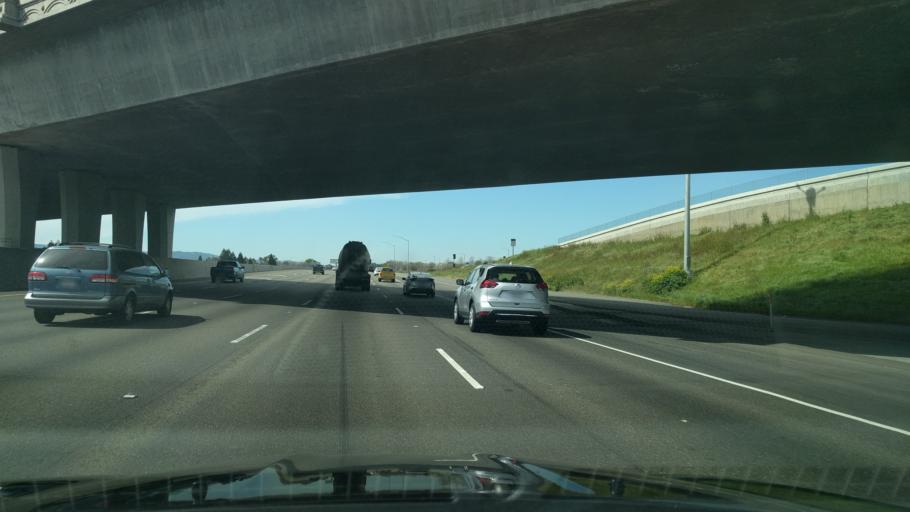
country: US
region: California
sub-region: Alameda County
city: Livermore
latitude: 37.7010
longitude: -121.8014
